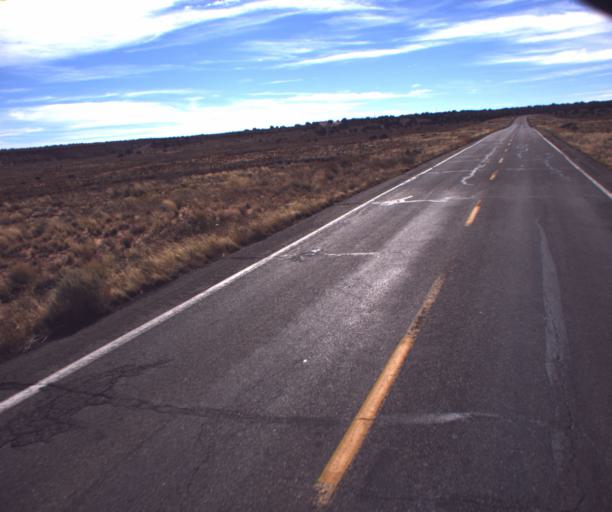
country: US
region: Arizona
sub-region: Coconino County
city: Kaibito
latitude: 36.6881
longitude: -111.2580
